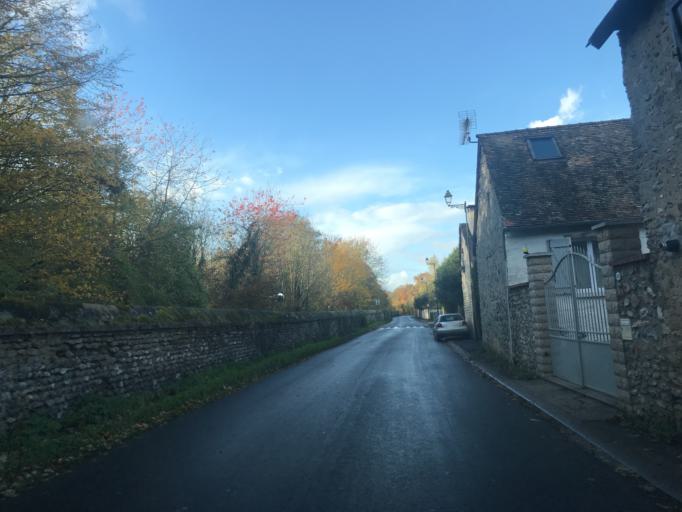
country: FR
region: Haute-Normandie
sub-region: Departement de l'Eure
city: Houlbec-Cocherel
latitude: 49.0776
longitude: 1.3030
